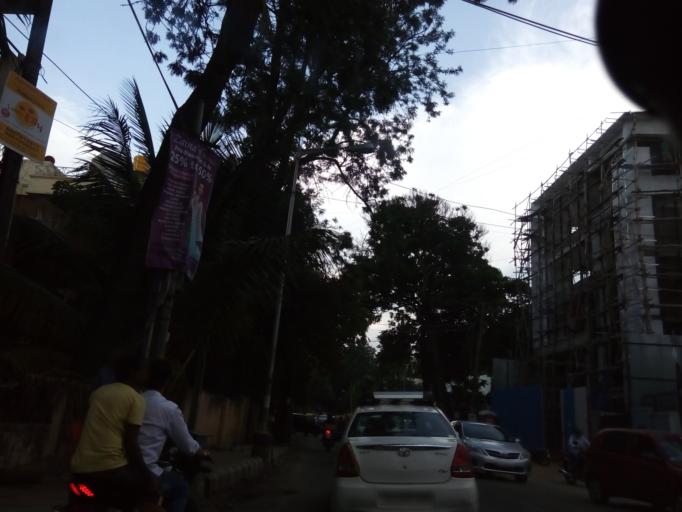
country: IN
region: Karnataka
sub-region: Bangalore Urban
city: Bangalore
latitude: 12.9998
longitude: 77.5998
